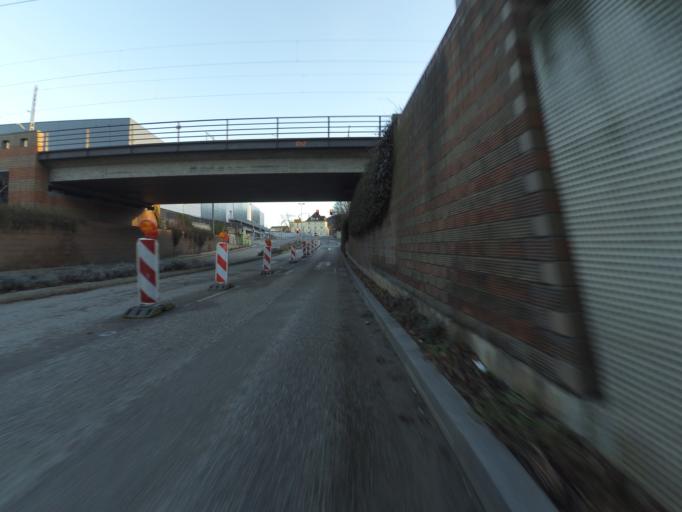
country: DE
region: Baden-Wuerttemberg
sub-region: Regierungsbezirk Stuttgart
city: Aalen
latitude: 48.8340
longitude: 10.0933
